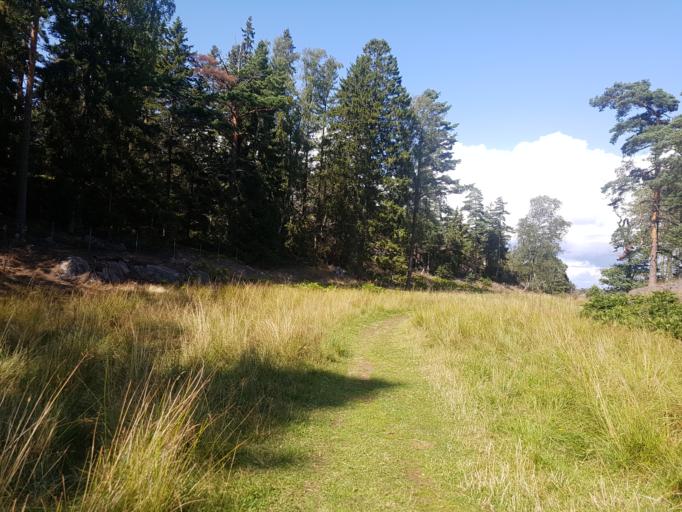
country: SE
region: Stockholm
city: Dalaro
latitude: 59.0453
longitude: 18.5207
